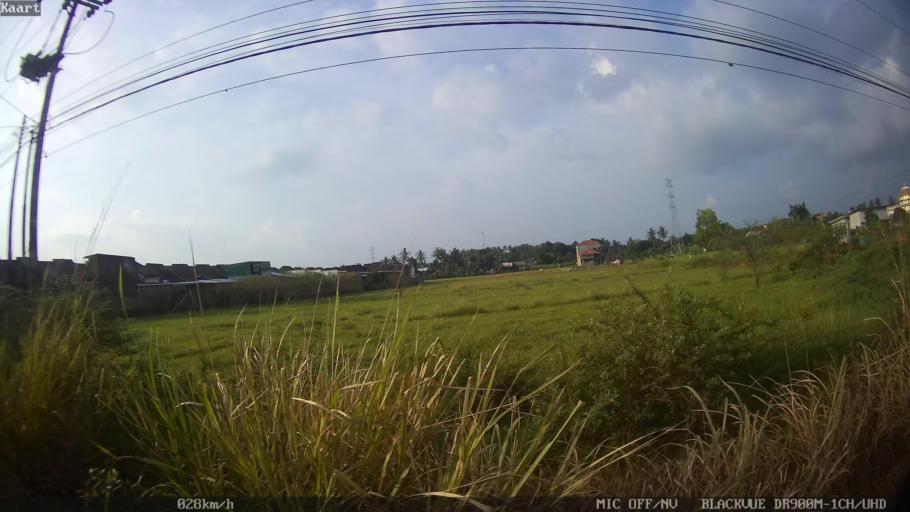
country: ID
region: Lampung
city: Kedaton
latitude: -5.3883
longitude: 105.3177
